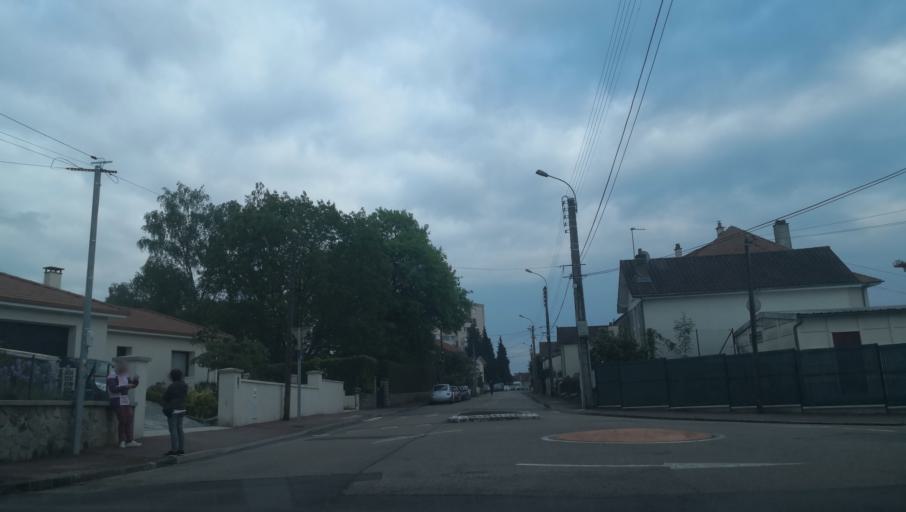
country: FR
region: Limousin
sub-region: Departement de la Haute-Vienne
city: Limoges
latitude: 45.8299
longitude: 1.2328
